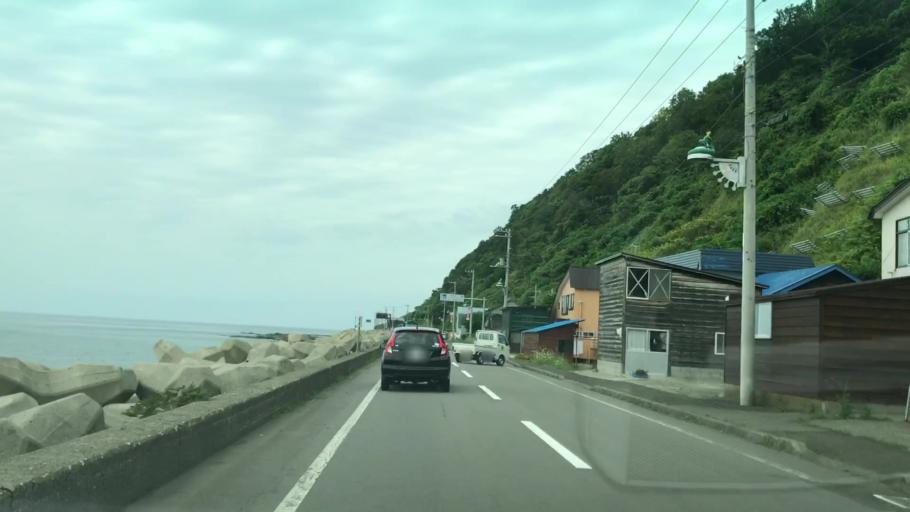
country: JP
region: Hokkaido
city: Iwanai
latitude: 43.1607
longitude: 140.3963
